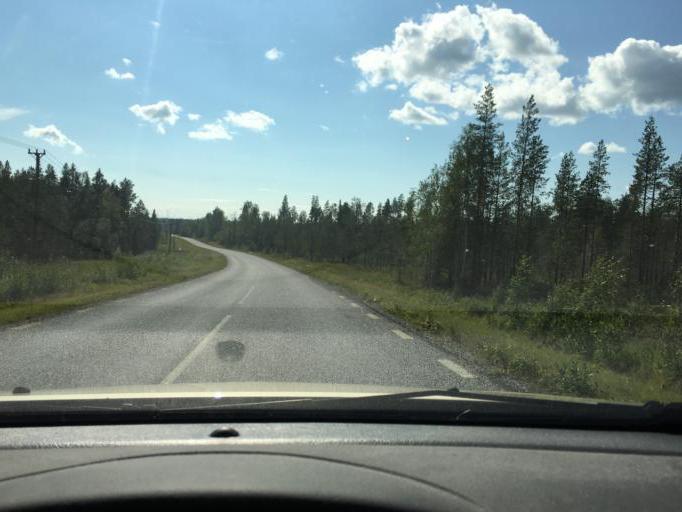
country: SE
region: Norrbotten
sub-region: Kalix Kommun
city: Toere
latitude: 66.0613
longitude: 22.6052
